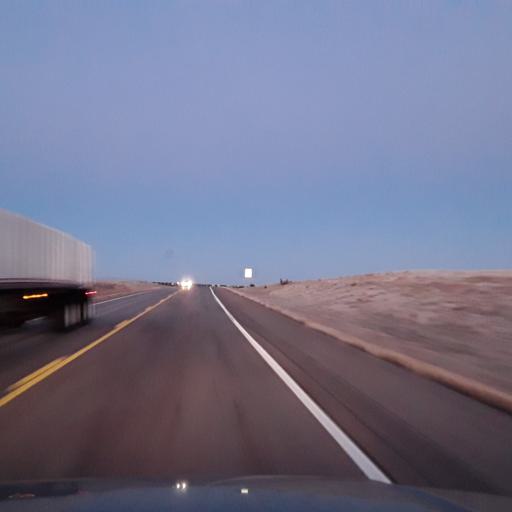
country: US
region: New Mexico
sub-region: Guadalupe County
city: Santa Rosa
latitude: 34.7453
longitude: -105.0183
